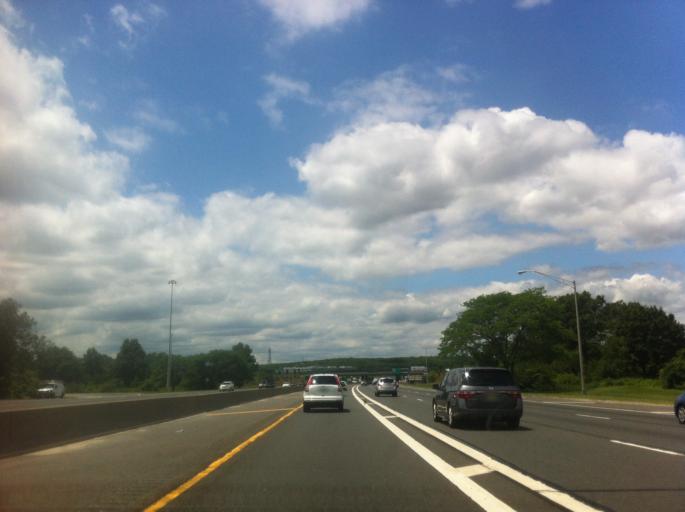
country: US
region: New York
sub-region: Suffolk County
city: Melville
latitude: 40.7813
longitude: -73.4134
